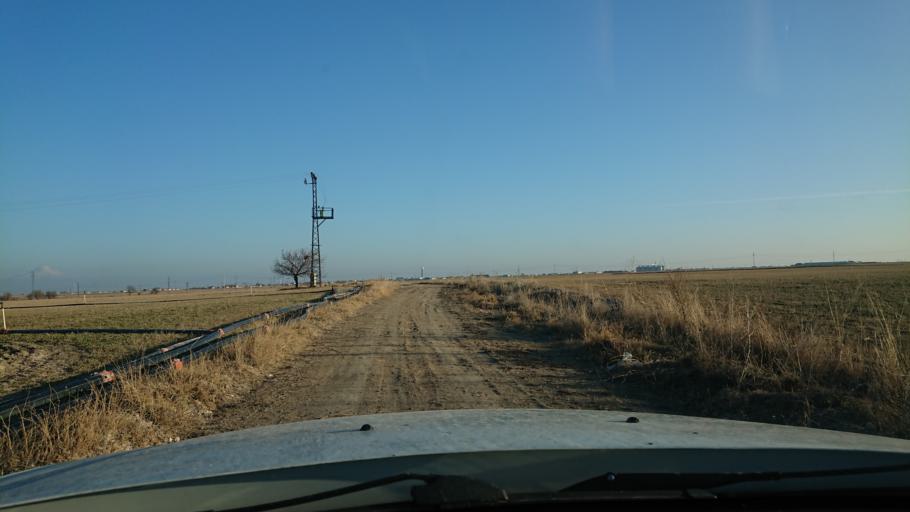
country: TR
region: Aksaray
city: Sultanhani
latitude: 38.2694
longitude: 33.5180
